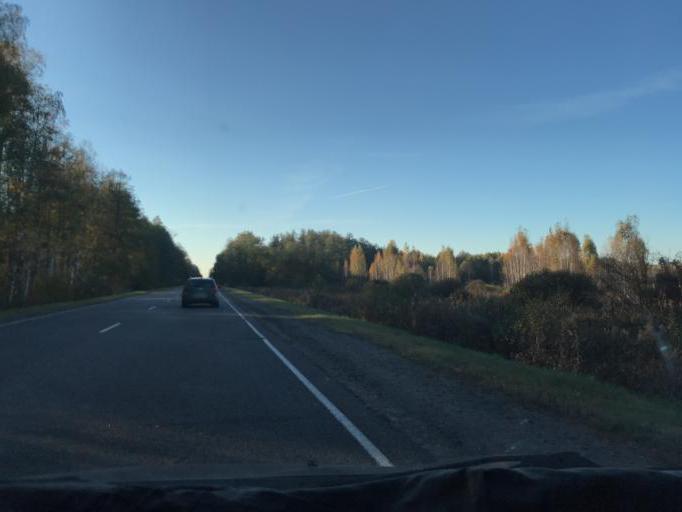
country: BY
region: Gomel
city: Pyetrykaw
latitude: 52.2641
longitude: 28.3107
